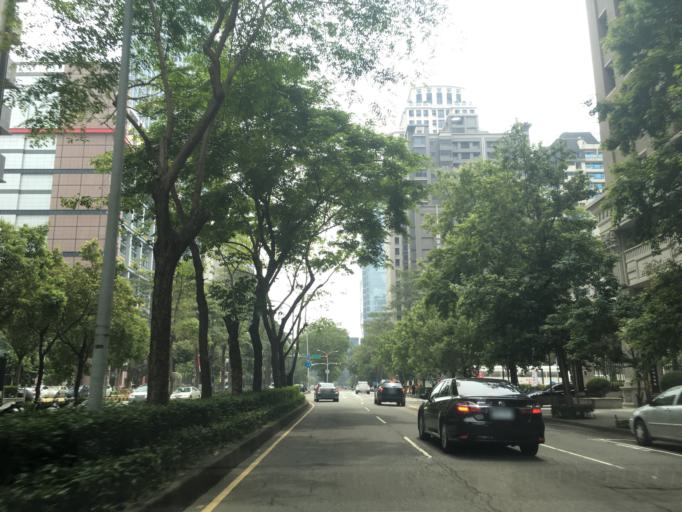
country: TW
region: Taiwan
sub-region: Taichung City
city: Taichung
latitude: 24.1647
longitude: 120.6414
